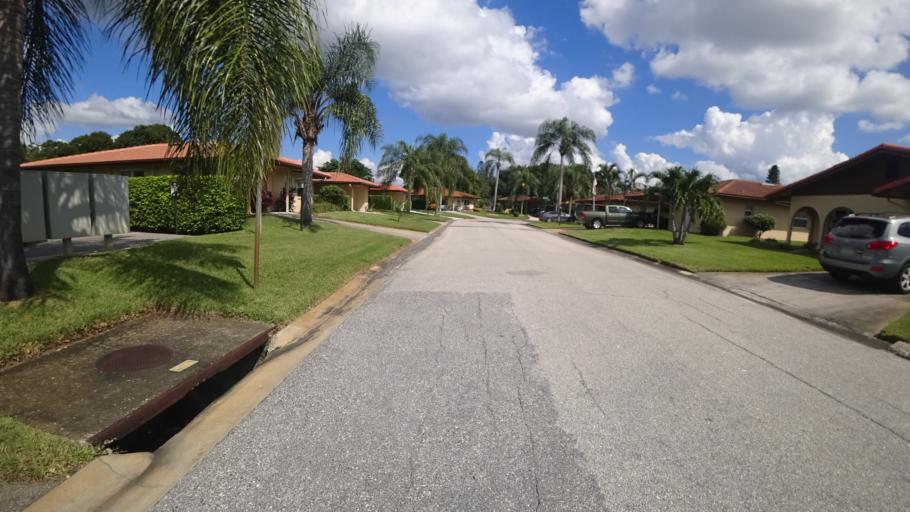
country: US
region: Florida
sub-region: Manatee County
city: Bayshore Gardens
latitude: 27.4278
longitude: -82.5931
